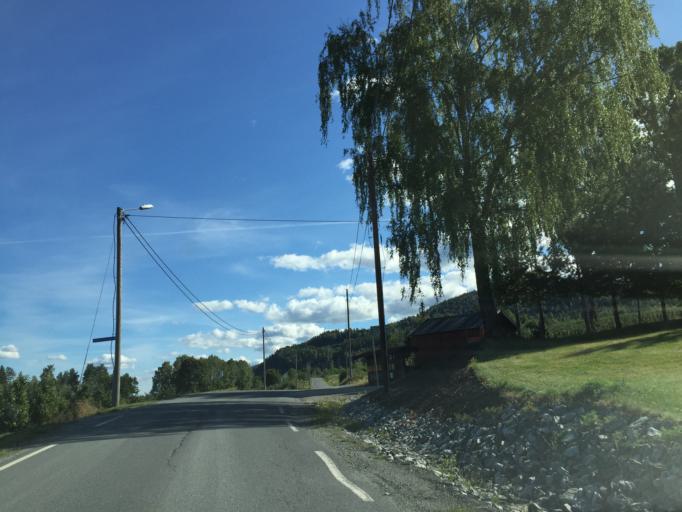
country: NO
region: Buskerud
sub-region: Ovre Eiker
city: Hokksund
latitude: 59.6923
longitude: 9.8448
